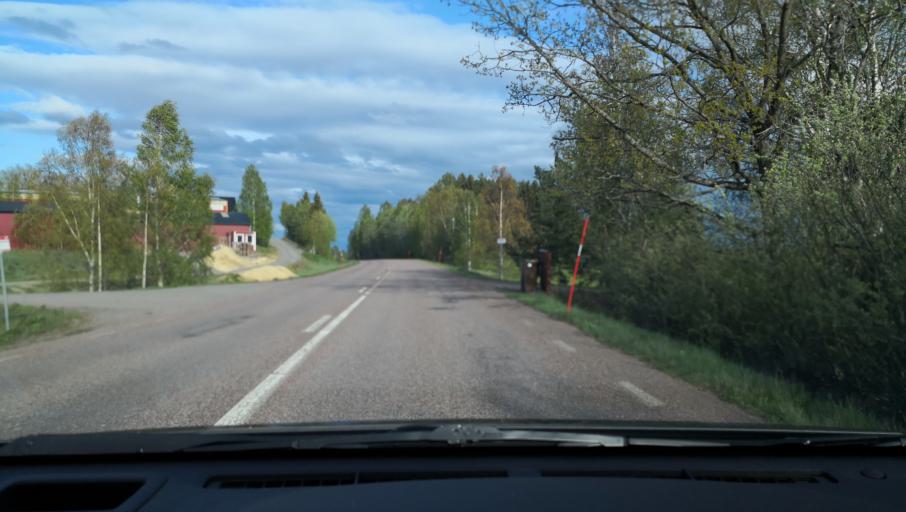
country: SE
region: Dalarna
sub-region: Hedemora Kommun
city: Hedemora
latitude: 60.2847
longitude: 15.9263
